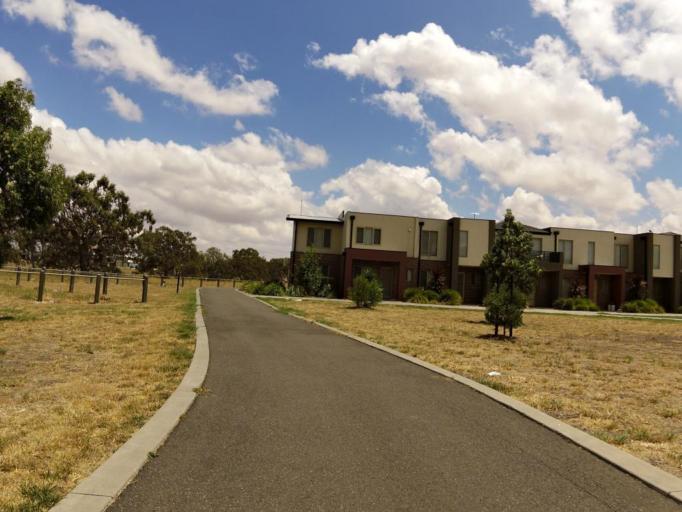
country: AU
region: Victoria
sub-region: Hume
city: Craigieburn
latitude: -37.5759
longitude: 144.9172
